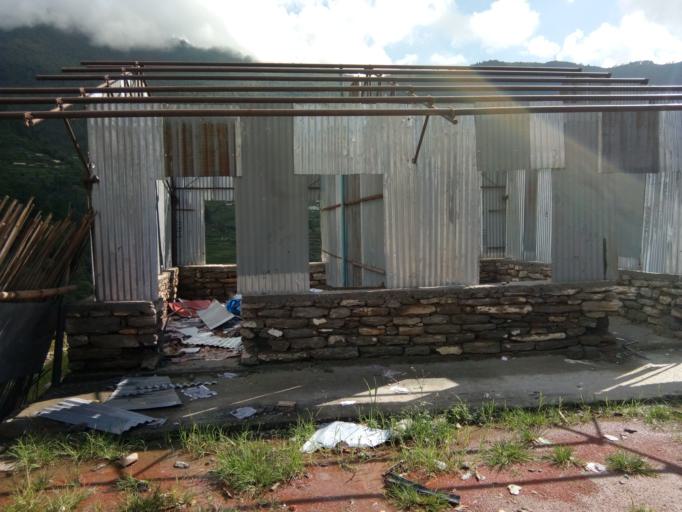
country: NP
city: Kodari
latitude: 27.7040
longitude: 85.9194
